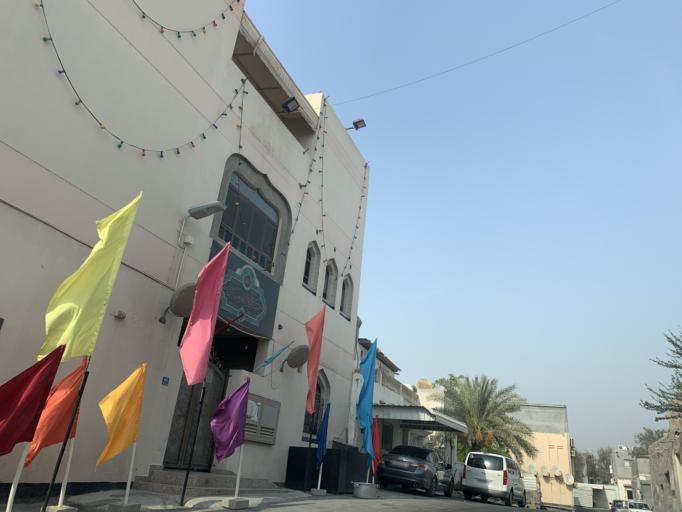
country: BH
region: Manama
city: Jidd Hafs
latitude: 26.2220
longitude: 50.4871
